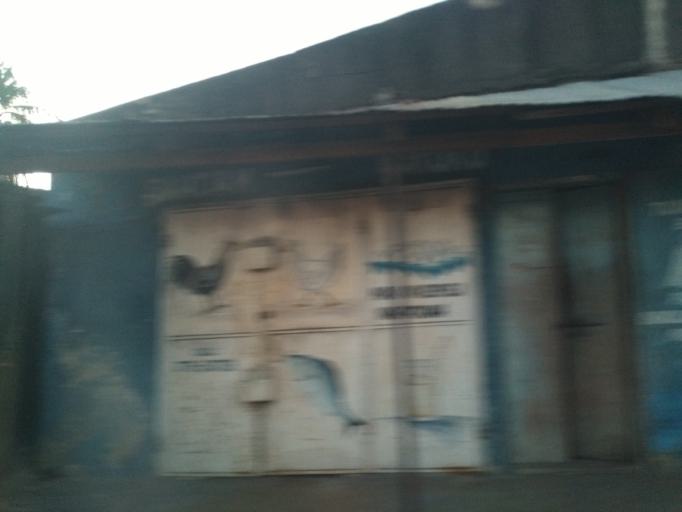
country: TZ
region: Dar es Salaam
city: Magomeni
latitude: -6.7680
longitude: 39.2677
